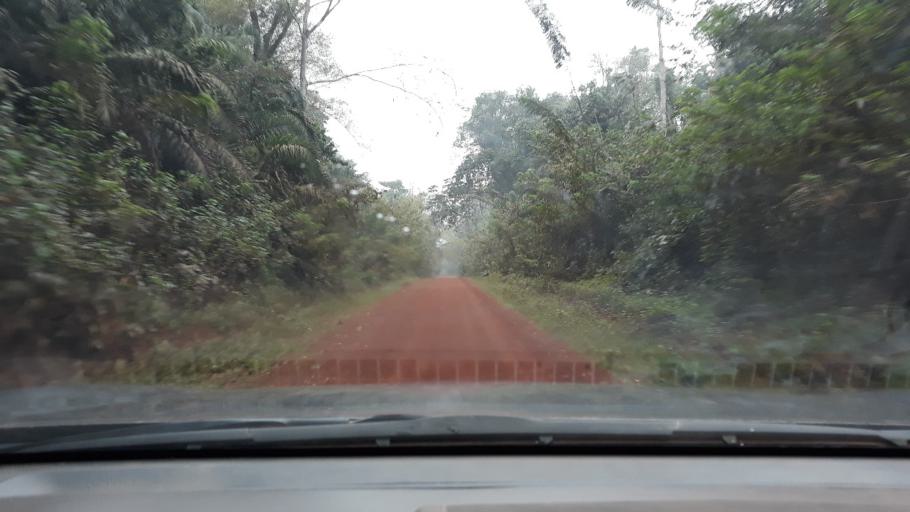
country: CD
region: Eastern Province
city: Aketi
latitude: 3.1219
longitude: 24.1232
